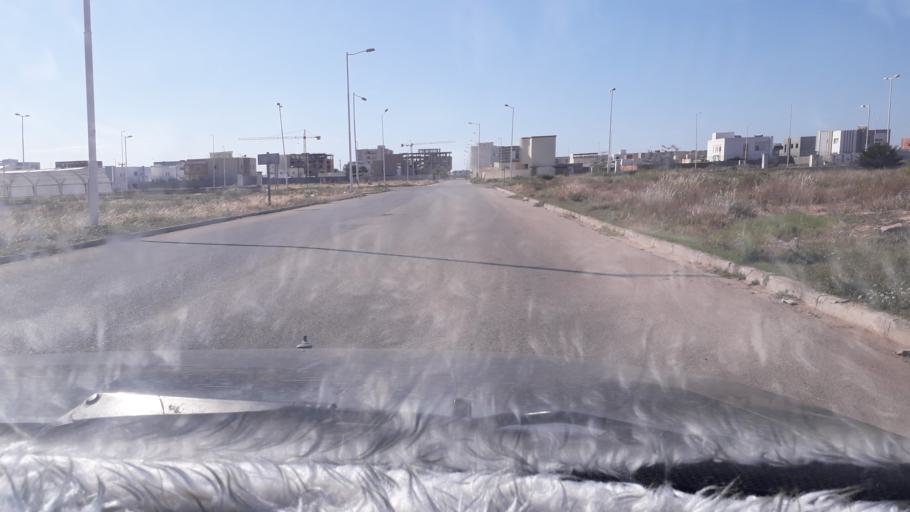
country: TN
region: Safaqis
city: Al Qarmadah
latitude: 34.8371
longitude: 10.7553
